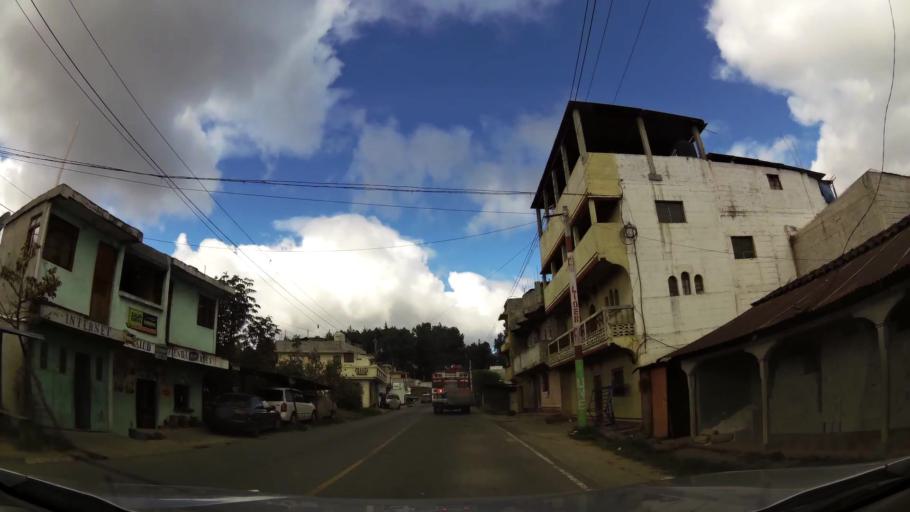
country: GT
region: Quiche
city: Chichicastenango
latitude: 14.9072
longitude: -91.1073
